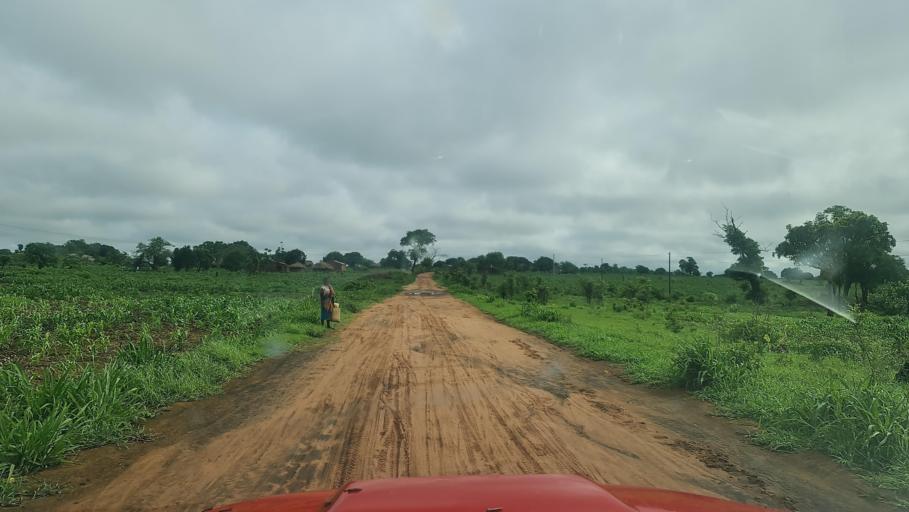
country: MW
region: Southern Region
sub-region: Nsanje District
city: Nsanje
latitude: -17.2074
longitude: 35.6810
